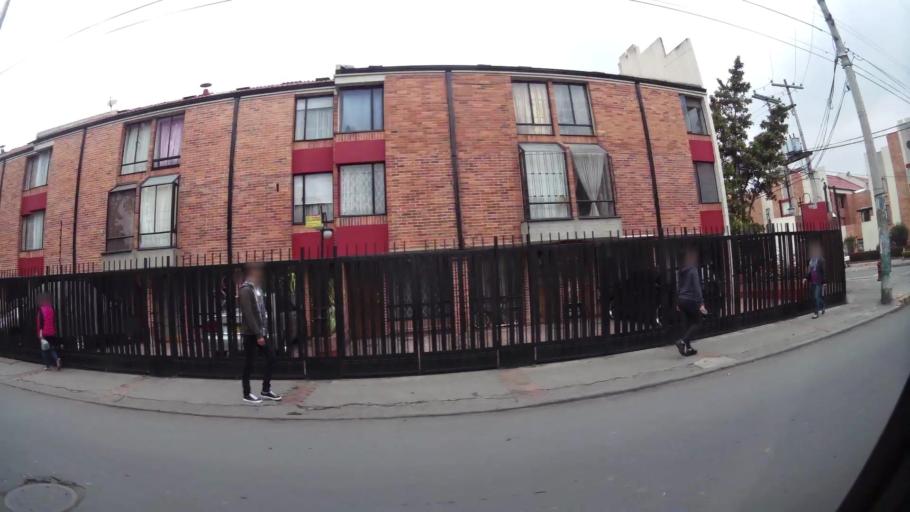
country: CO
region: Cundinamarca
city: Cota
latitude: 4.7475
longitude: -74.0568
